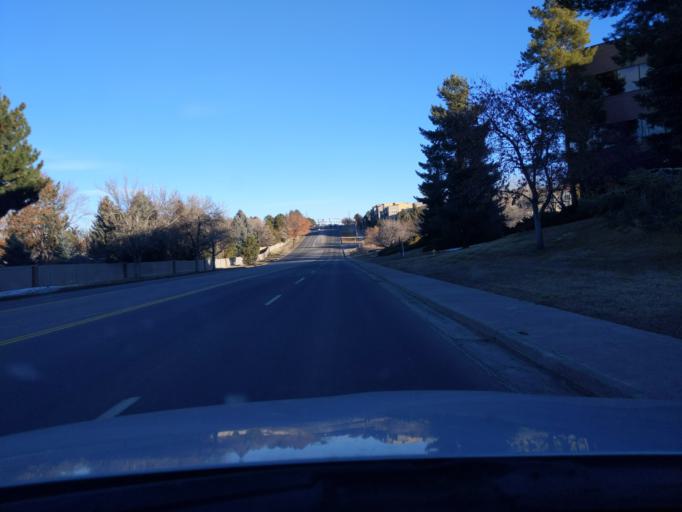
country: US
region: Colorado
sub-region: Arapahoe County
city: Centennial
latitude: 39.5764
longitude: -104.8856
